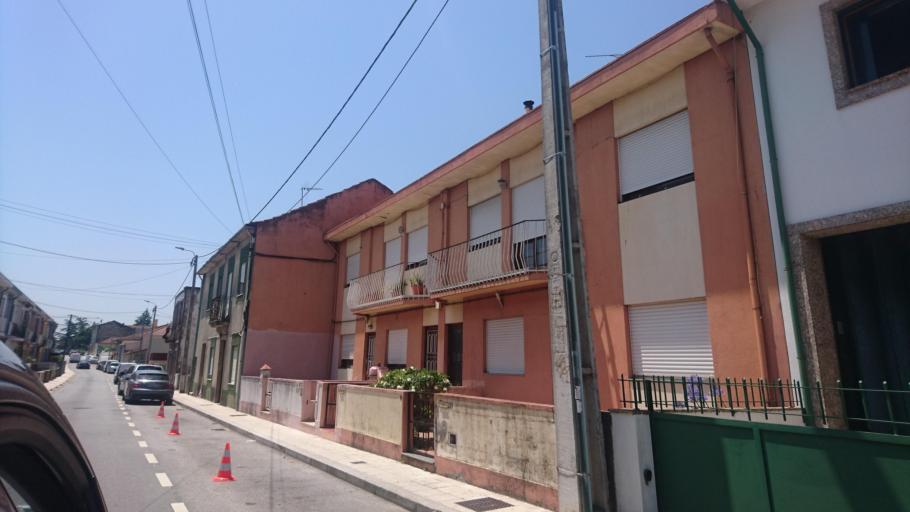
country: PT
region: Porto
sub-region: Gondomar
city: Rio Tinto
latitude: 41.1620
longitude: -8.5483
